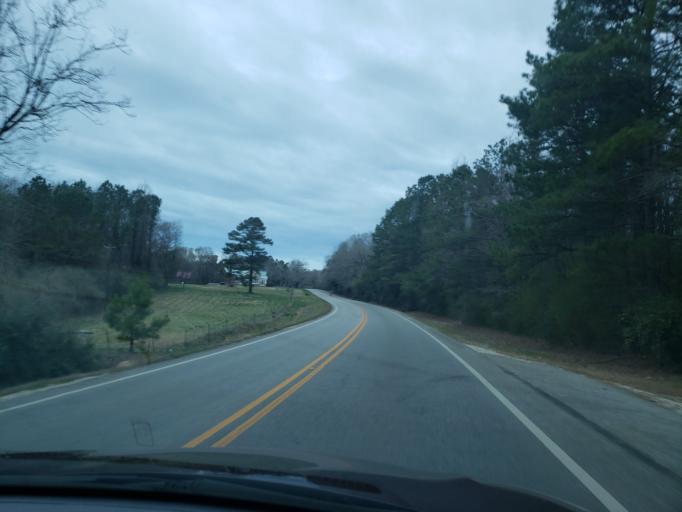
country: US
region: Alabama
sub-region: Chambers County
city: Lafayette
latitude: 32.9345
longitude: -85.3951
